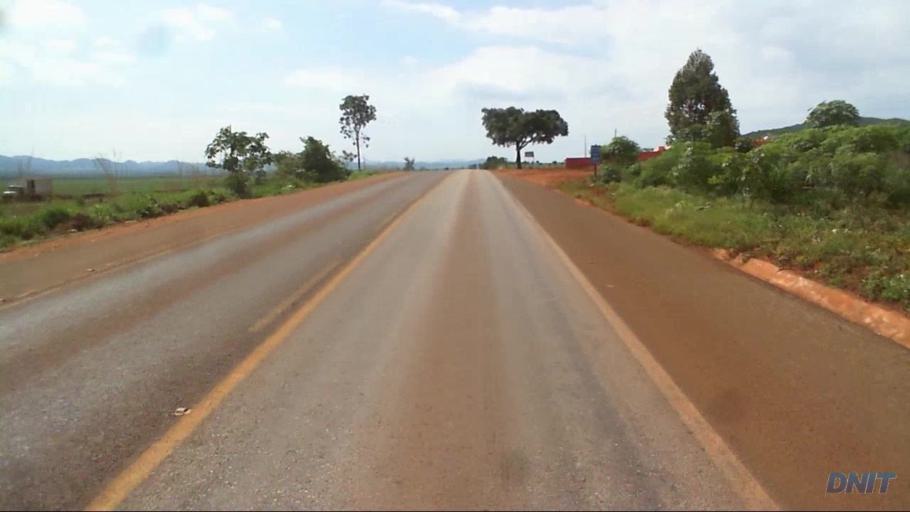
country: BR
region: Goias
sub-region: Barro Alto
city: Barro Alto
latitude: -14.9992
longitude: -48.9053
